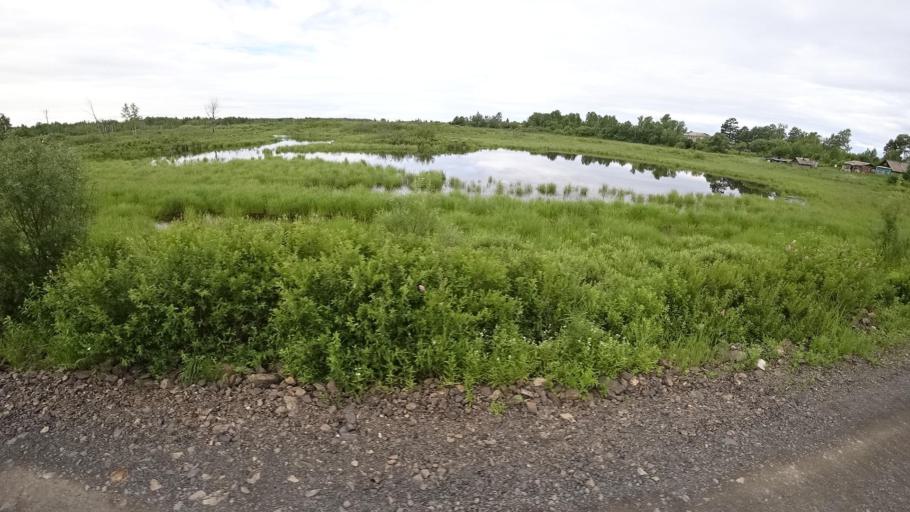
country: RU
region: Khabarovsk Krai
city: Amursk
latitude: 49.9024
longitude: 136.1460
